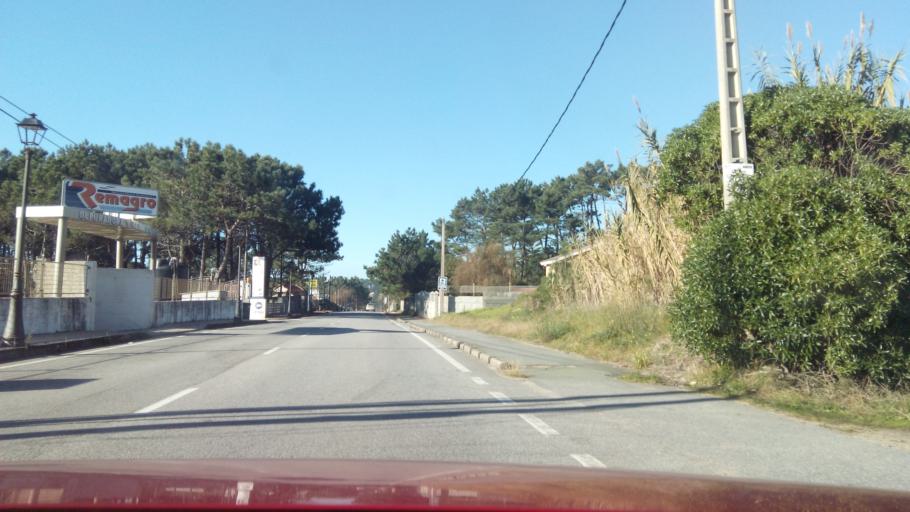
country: ES
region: Galicia
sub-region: Provincia de Pontevedra
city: O Grove
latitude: 42.4591
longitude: -8.8909
